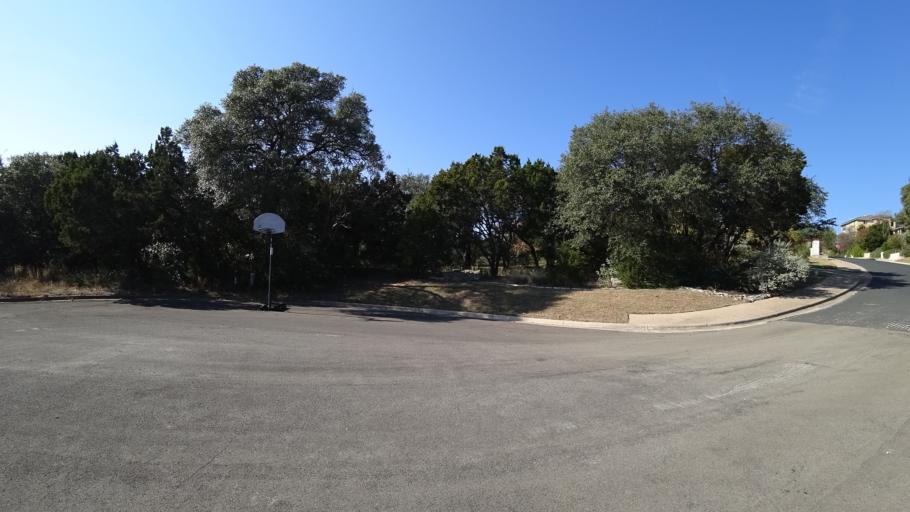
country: US
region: Texas
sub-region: Williamson County
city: Jollyville
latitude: 30.3935
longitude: -97.7744
